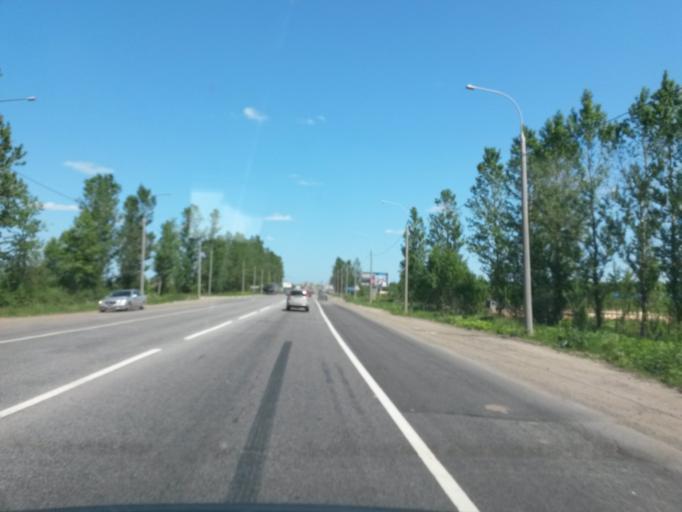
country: RU
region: Jaroslavl
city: Yaroslavl
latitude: 57.6594
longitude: 39.7568
